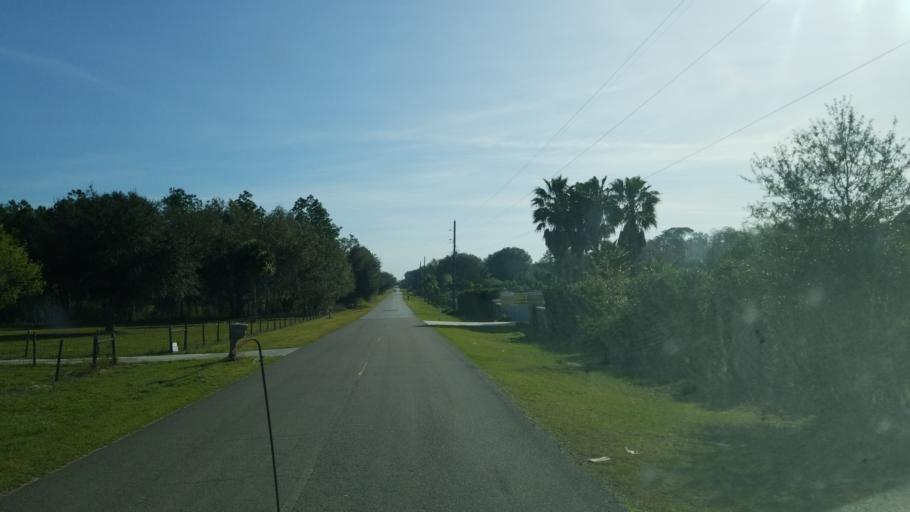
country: US
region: Florida
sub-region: Lake County
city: Clermont
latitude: 28.4615
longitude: -81.7909
